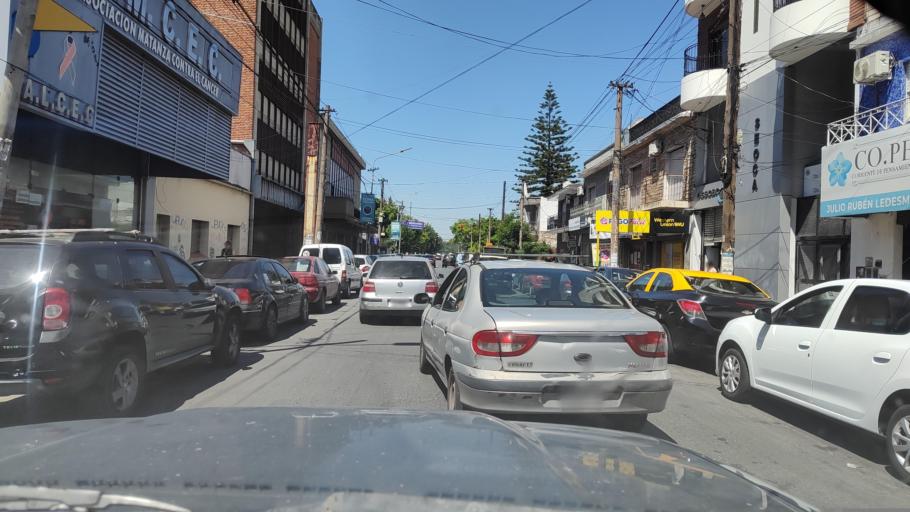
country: AR
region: Buenos Aires
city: San Justo
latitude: -34.6798
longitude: -58.5624
